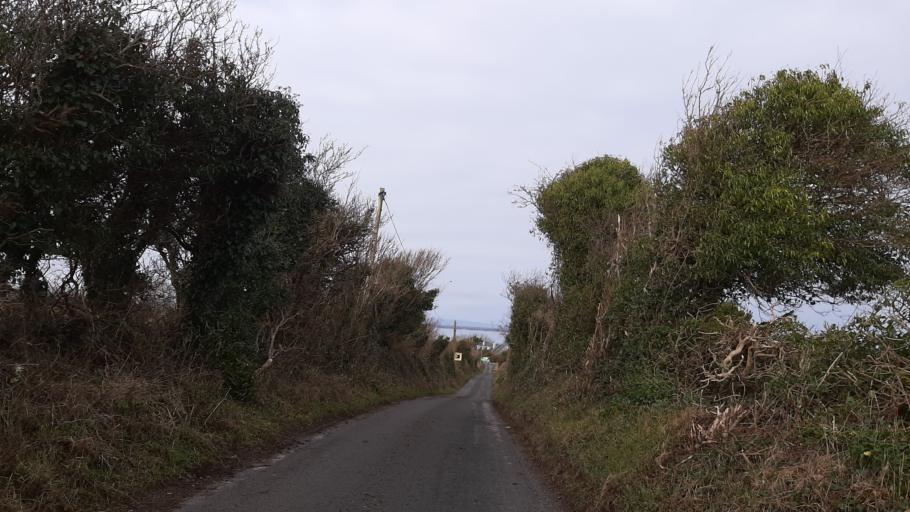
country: IE
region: Connaught
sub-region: County Galway
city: Gaillimh
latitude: 53.3161
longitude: -9.0544
